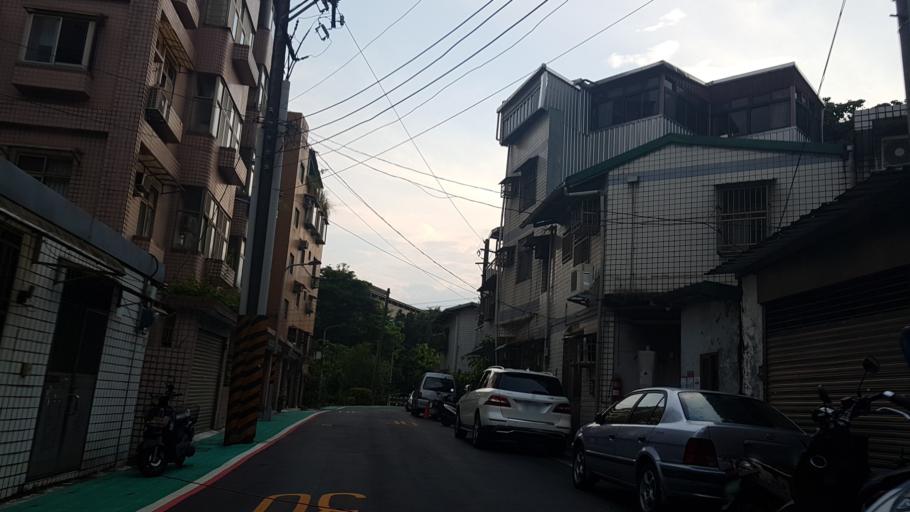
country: TW
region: Taipei
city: Taipei
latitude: 25.0057
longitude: 121.5419
